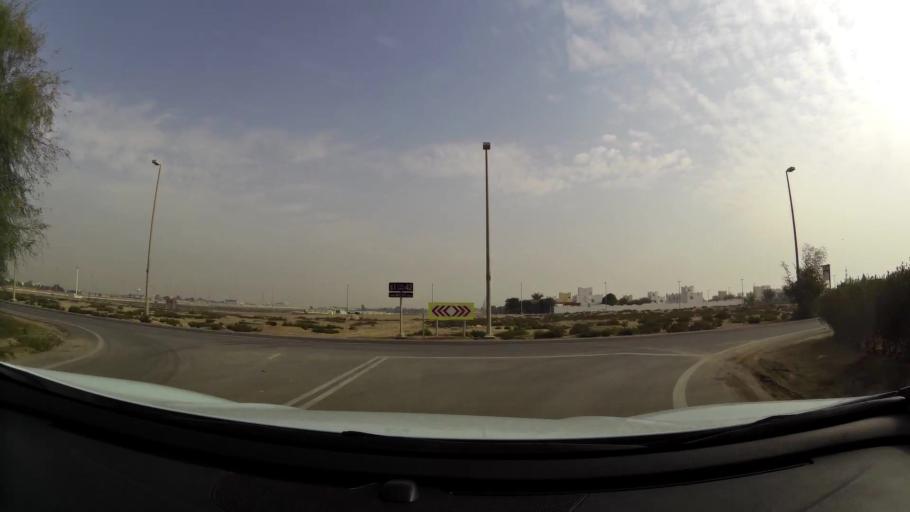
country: AE
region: Abu Dhabi
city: Abu Dhabi
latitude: 24.6685
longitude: 54.7657
